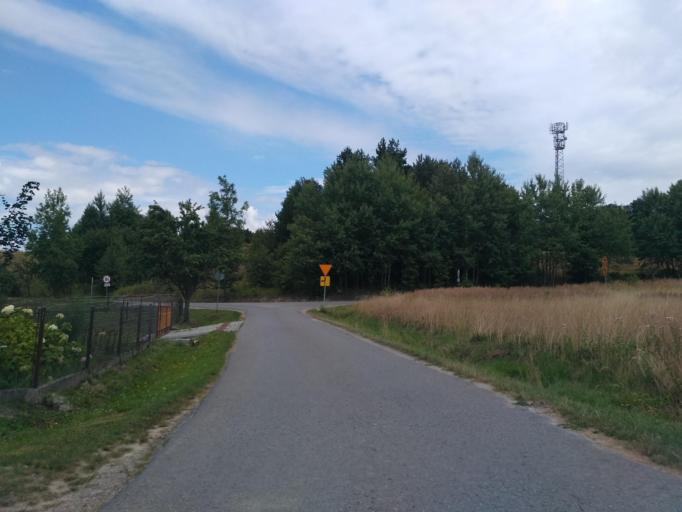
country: PL
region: Subcarpathian Voivodeship
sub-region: Powiat rzeszowski
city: Hyzne
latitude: 49.8987
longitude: 22.2297
